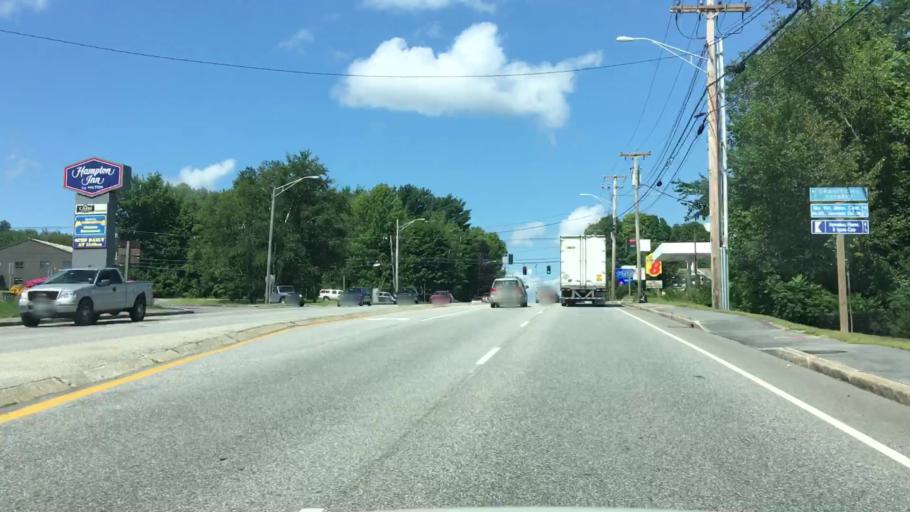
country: US
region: Maine
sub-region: Kennebec County
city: Augusta
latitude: 44.3176
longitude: -69.8152
